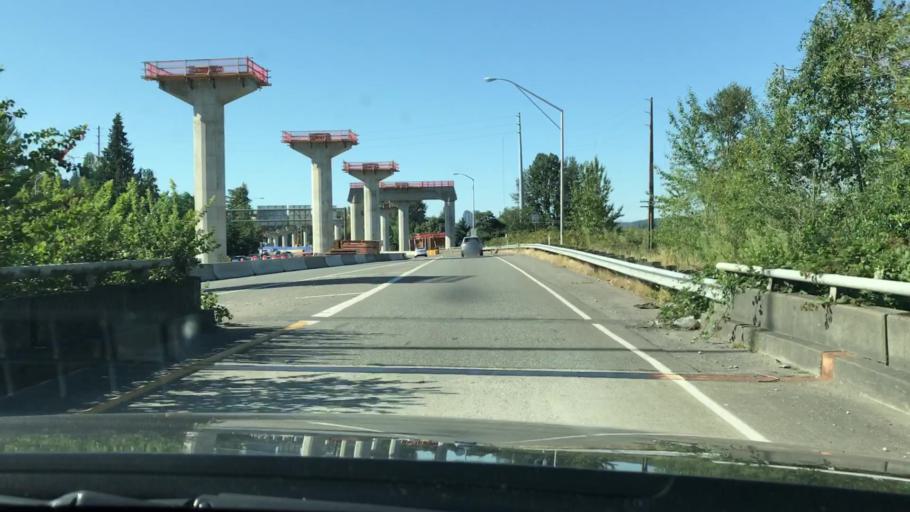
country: US
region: Washington
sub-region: King County
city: Newport
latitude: 47.5812
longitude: -122.1875
